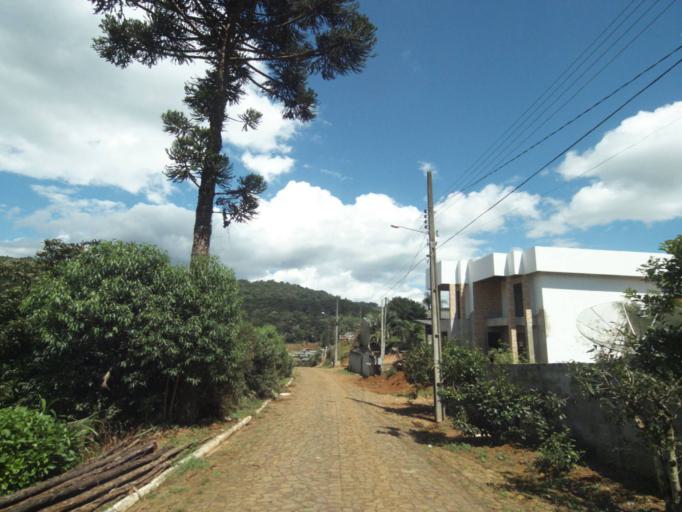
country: BR
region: Parana
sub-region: Uniao Da Vitoria
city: Uniao da Vitoria
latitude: -26.1711
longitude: -51.5508
